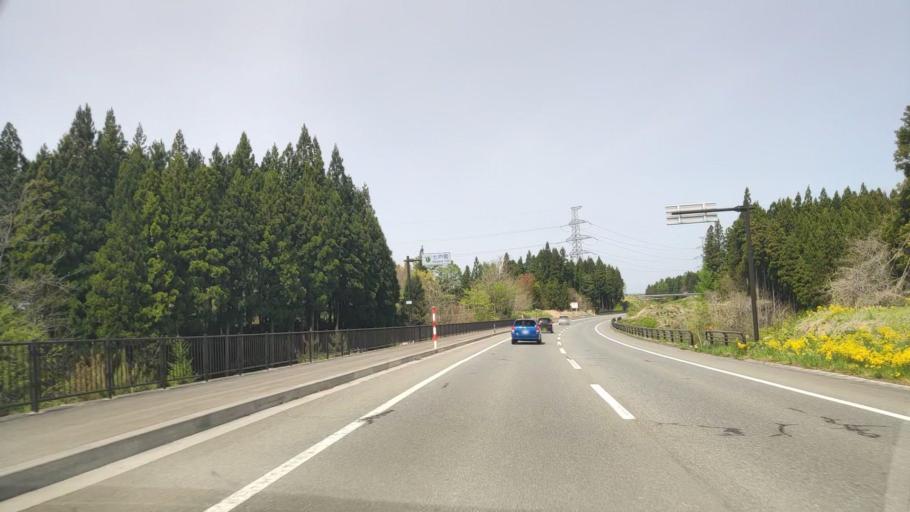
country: JP
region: Aomori
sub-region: Misawa Shi
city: Inuotose
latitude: 40.6804
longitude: 141.1711
